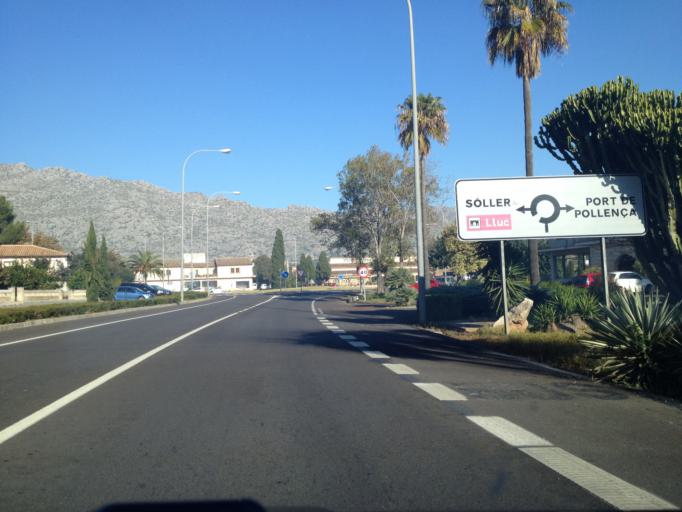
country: ES
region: Balearic Islands
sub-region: Illes Balears
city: Pollenca
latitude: 39.8834
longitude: 3.0228
